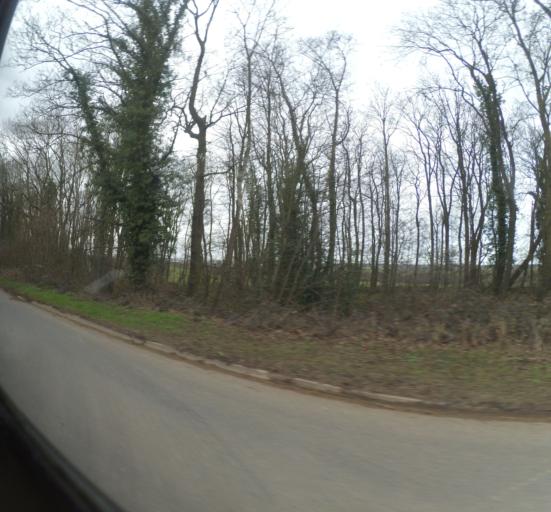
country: GB
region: England
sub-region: Warwickshire
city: Brandon
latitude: 52.4122
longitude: -1.3810
